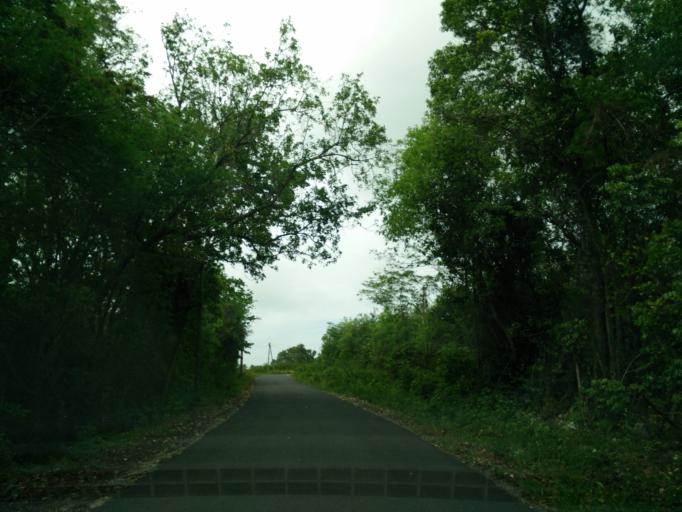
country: GP
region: Guadeloupe
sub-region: Guadeloupe
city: Grand-Bourg
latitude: 15.9114
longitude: -61.2763
